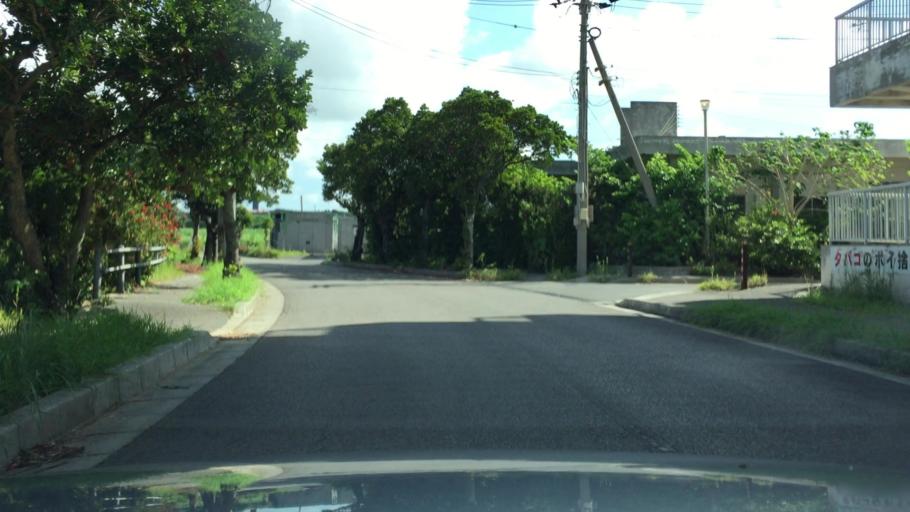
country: JP
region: Okinawa
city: Ishigaki
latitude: 24.3504
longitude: 124.1647
